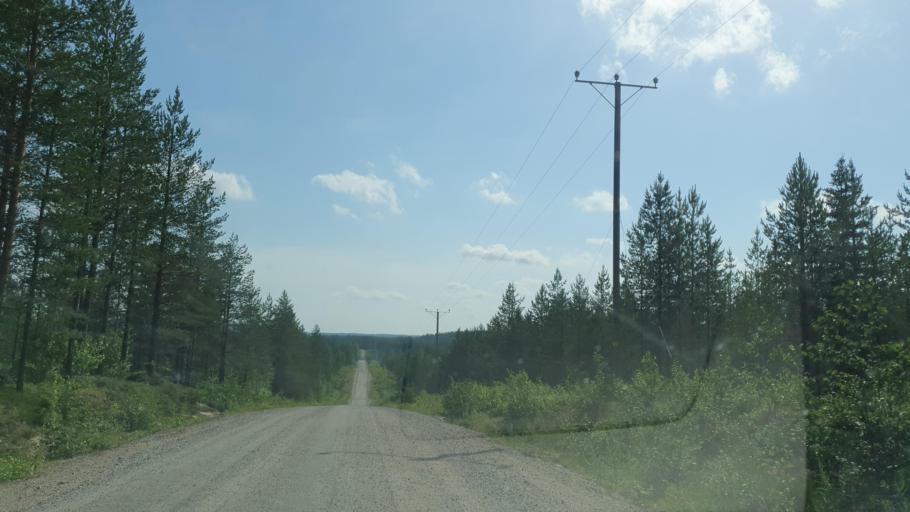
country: FI
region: Kainuu
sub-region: Kehys-Kainuu
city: Kuhmo
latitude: 64.0262
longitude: 29.9221
